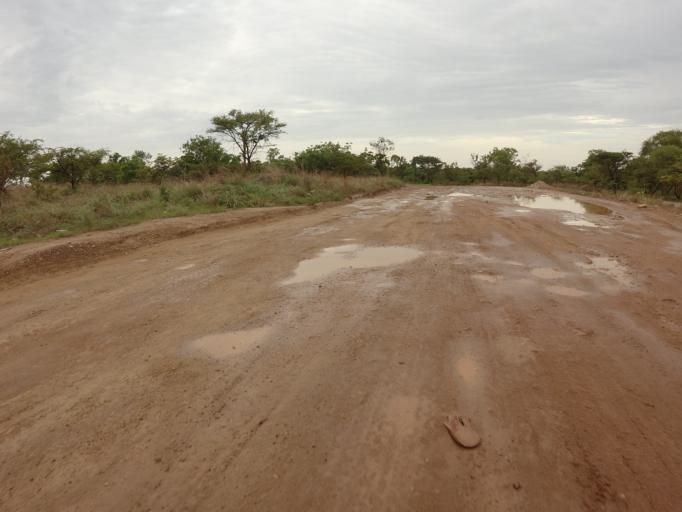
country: GH
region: Upper East
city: Bolgatanga
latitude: 10.8743
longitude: -0.6391
